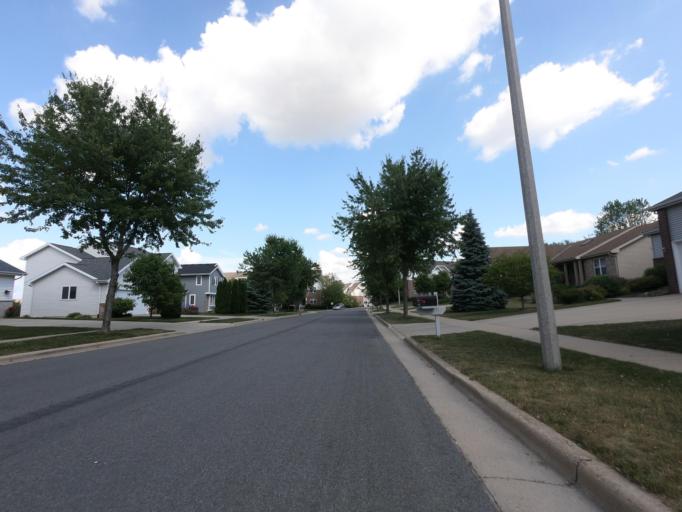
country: US
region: Wisconsin
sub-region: Dane County
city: Middleton
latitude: 43.0759
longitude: -89.5535
